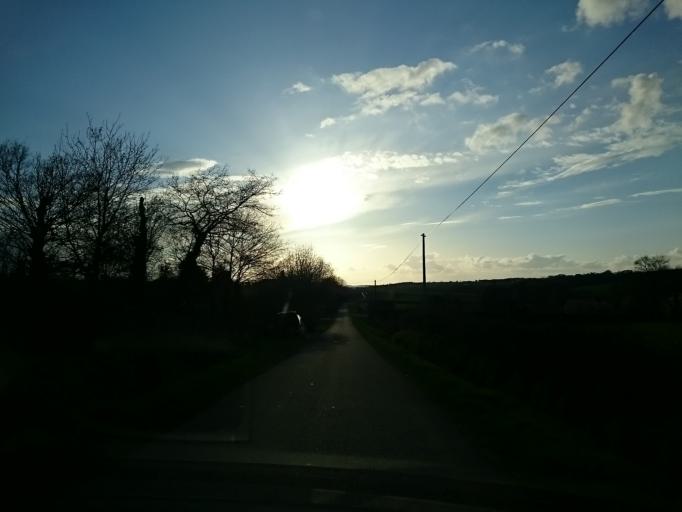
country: FR
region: Brittany
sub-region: Departement d'Ille-et-Vilaine
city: Crevin
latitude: 47.9223
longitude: -1.6519
